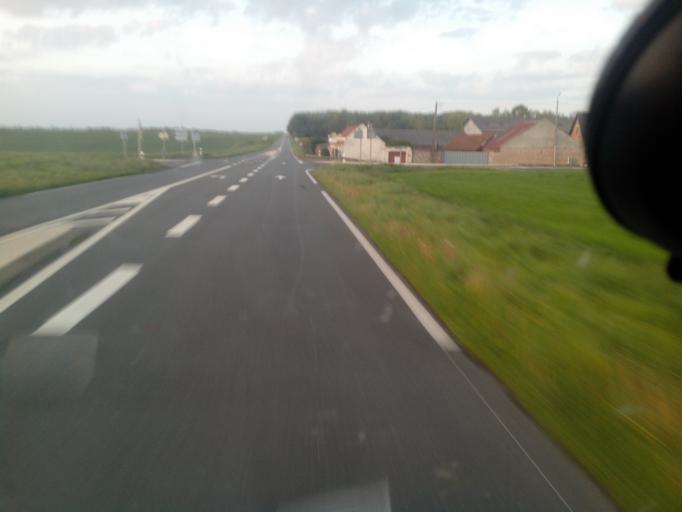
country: FR
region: Picardie
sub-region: Departement de la Somme
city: Crecy-en-Ponthieu
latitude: 50.2128
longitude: 1.9103
